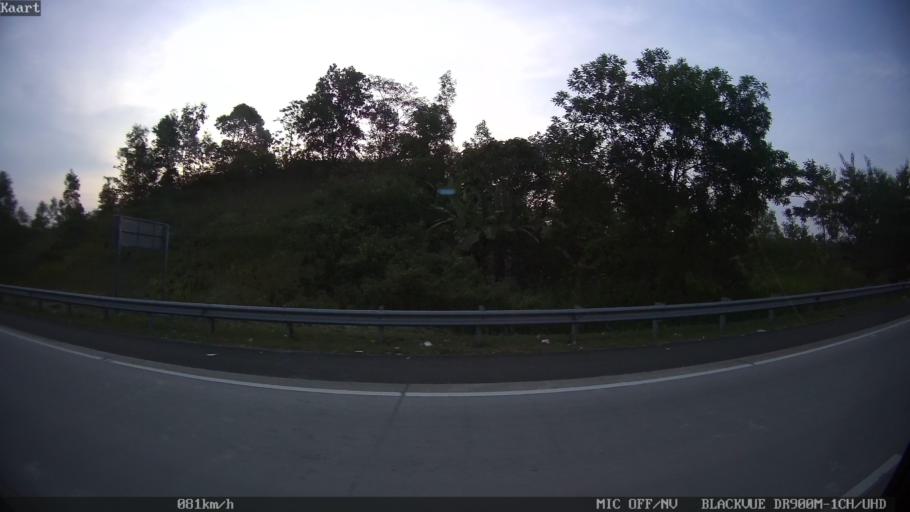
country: ID
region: Lampung
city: Penengahan
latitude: -5.8359
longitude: 105.7304
